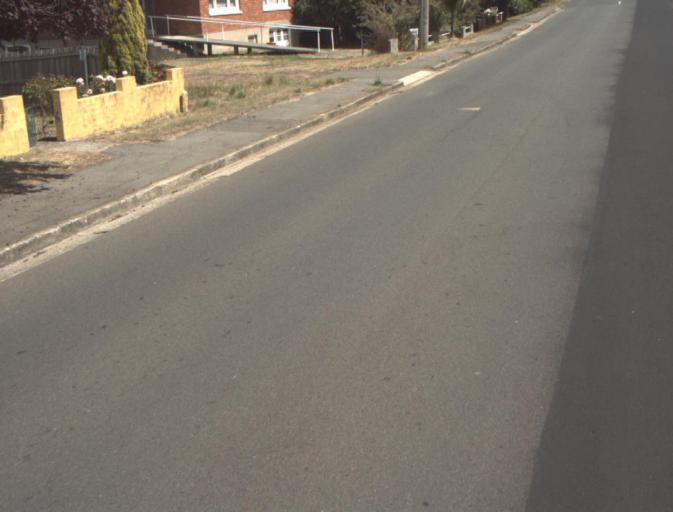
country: AU
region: Tasmania
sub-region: Launceston
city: Newstead
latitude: -41.4198
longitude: 147.1661
